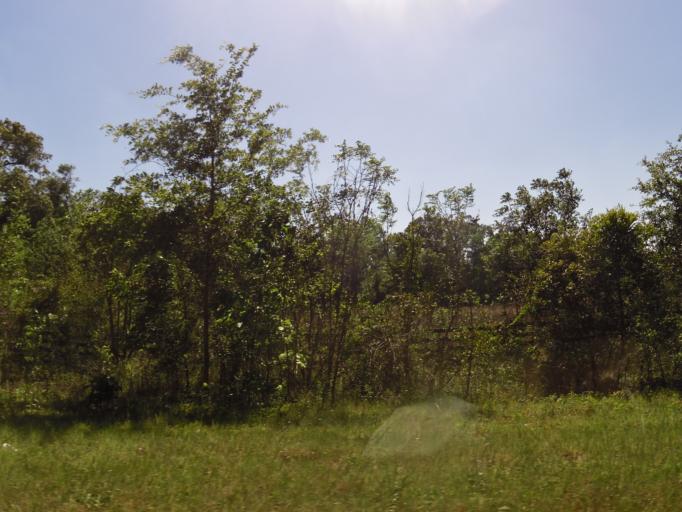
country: US
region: South Carolina
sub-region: Barnwell County
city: Williston
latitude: 33.4287
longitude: -81.4814
